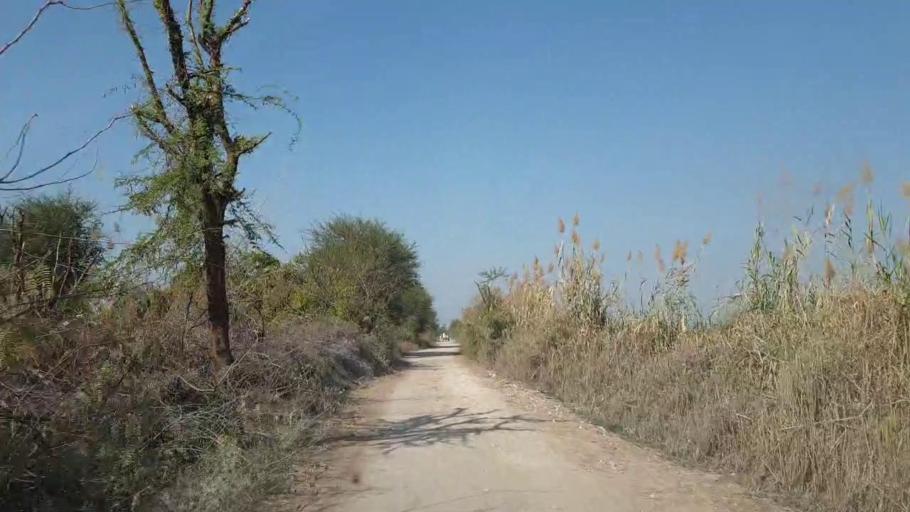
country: PK
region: Sindh
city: Mirpur Khas
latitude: 25.7202
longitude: 69.1393
